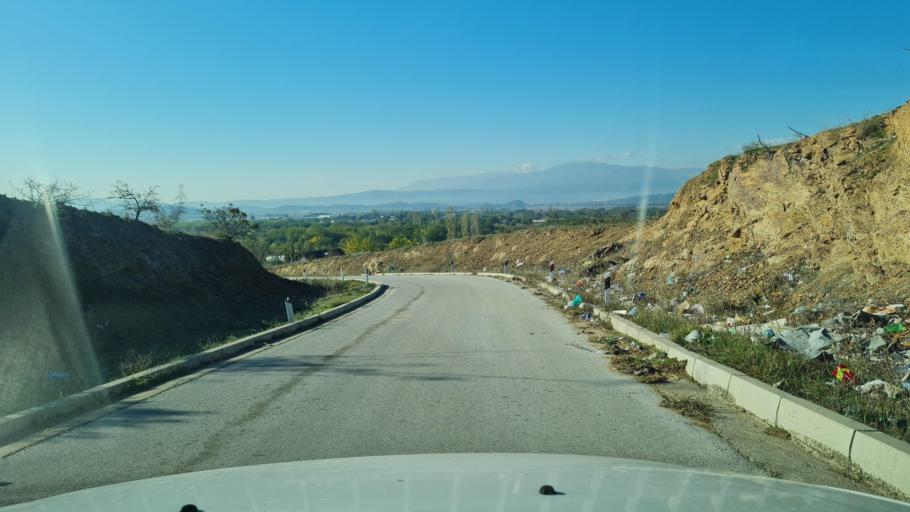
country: MK
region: Bogdanci
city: Bogdanci
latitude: 41.1950
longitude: 22.5635
